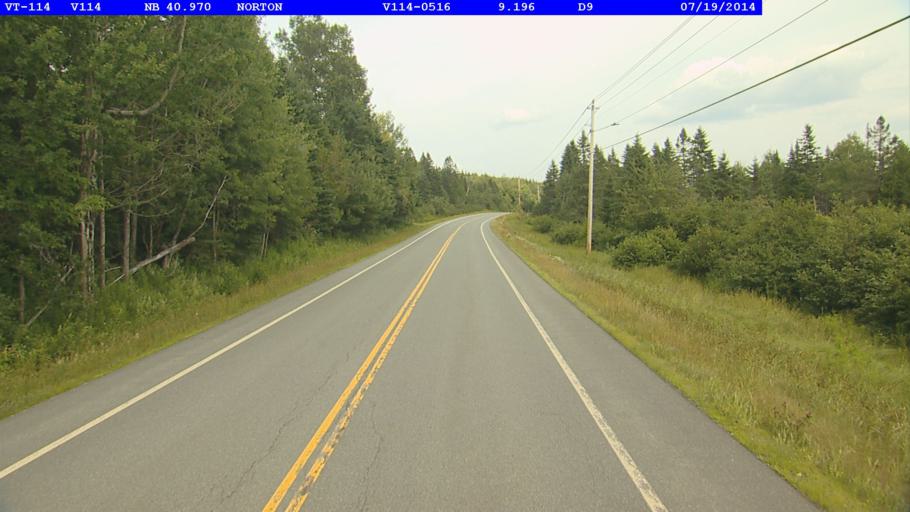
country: CA
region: Quebec
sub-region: Estrie
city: Coaticook
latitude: 44.9960
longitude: -71.7218
